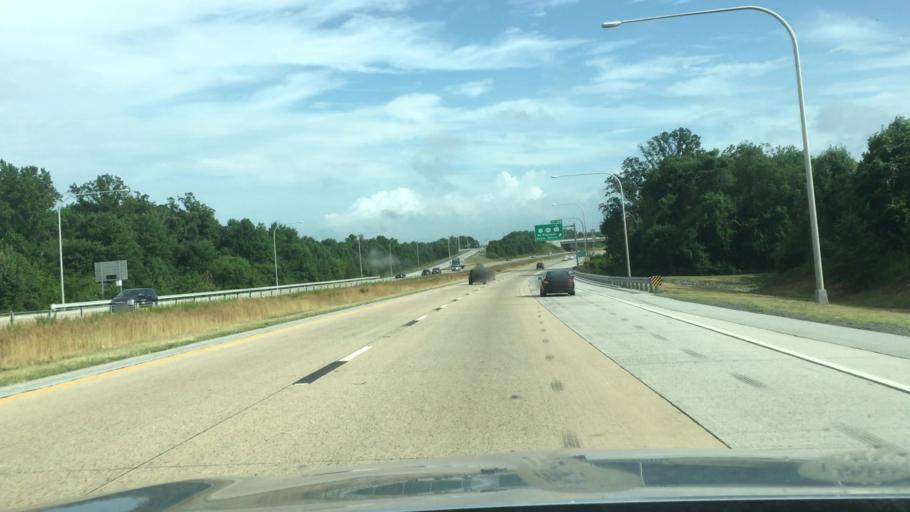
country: US
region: Delaware
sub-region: New Castle County
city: Middletown
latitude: 39.5063
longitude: -75.6470
